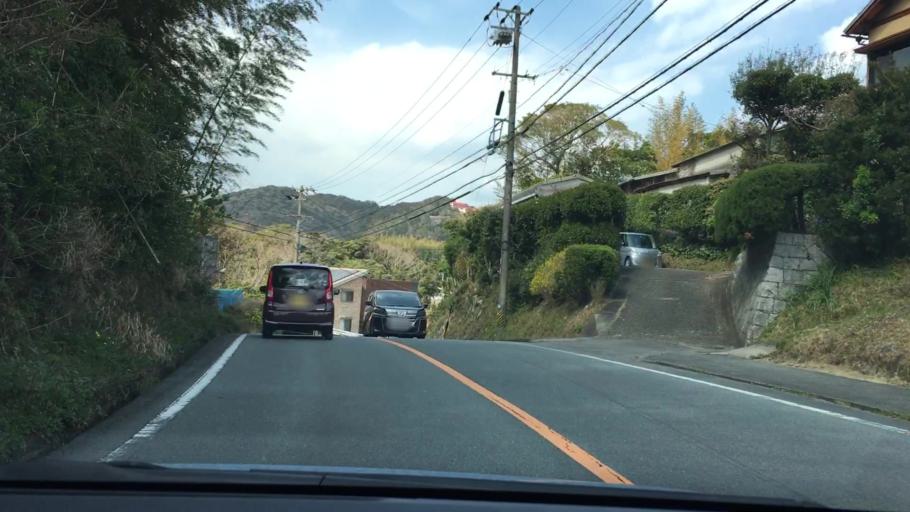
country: JP
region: Mie
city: Toba
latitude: 34.4588
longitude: 136.8643
